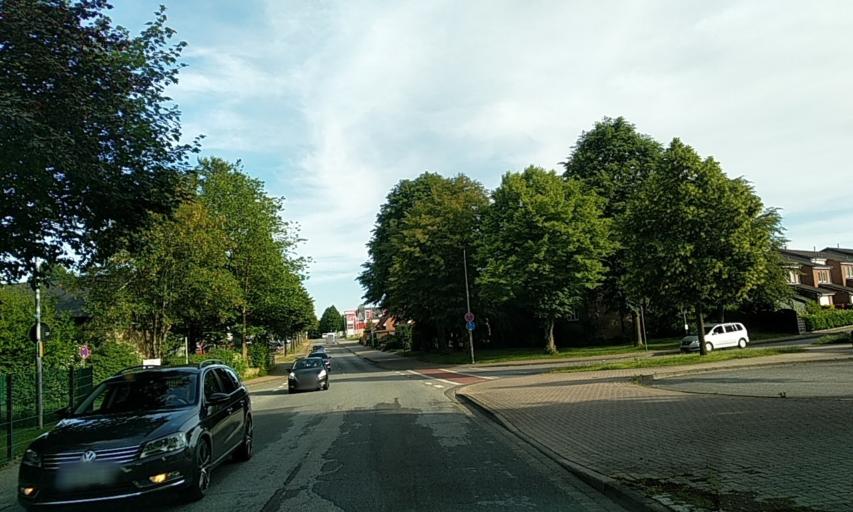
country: DE
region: Schleswig-Holstein
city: Schleswig
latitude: 54.5236
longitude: 9.5617
